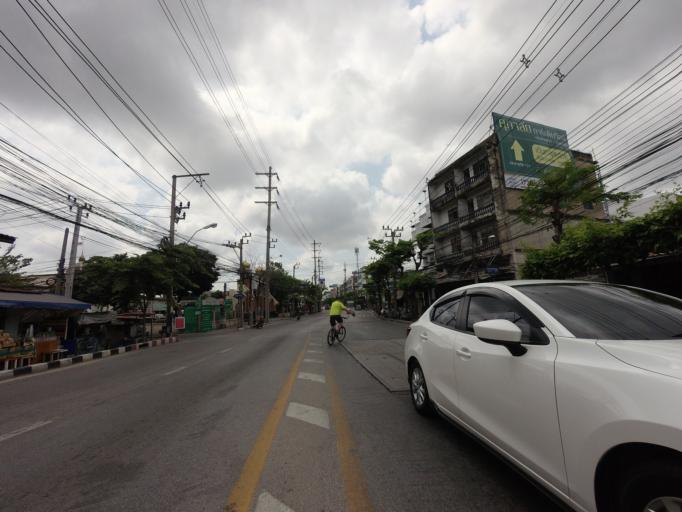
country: TH
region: Bangkok
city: Thung Khru
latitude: 13.6417
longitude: 100.4998
